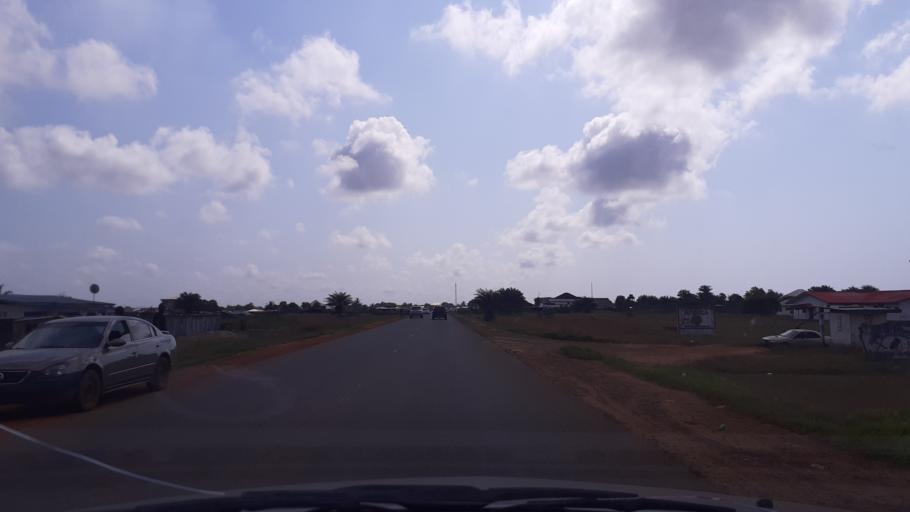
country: LR
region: Montserrado
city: Monrovia
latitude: 6.2201
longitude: -10.5929
